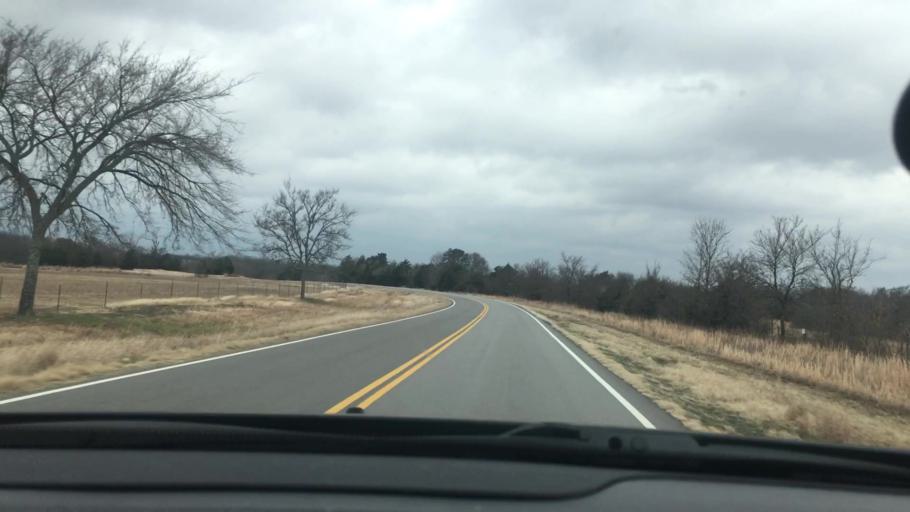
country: US
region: Oklahoma
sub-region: Atoka County
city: Atoka
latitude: 34.3775
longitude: -96.2631
